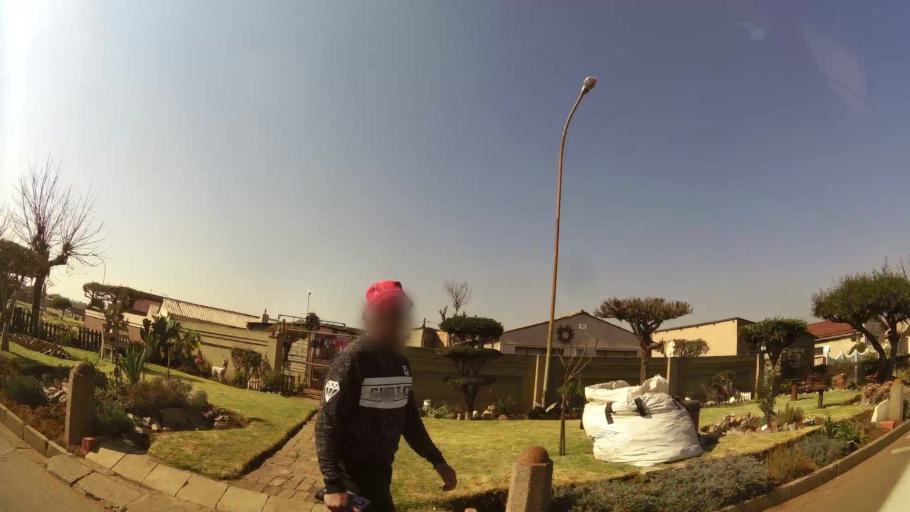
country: ZA
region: Gauteng
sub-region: Ekurhuleni Metropolitan Municipality
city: Benoni
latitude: -26.2224
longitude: 28.3028
